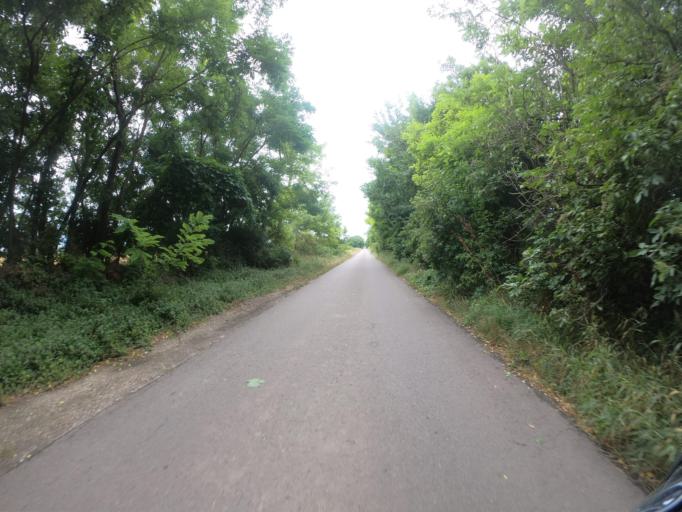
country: HU
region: Borsod-Abauj-Zemplen
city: Szentistvan
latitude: 47.7259
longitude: 20.6858
